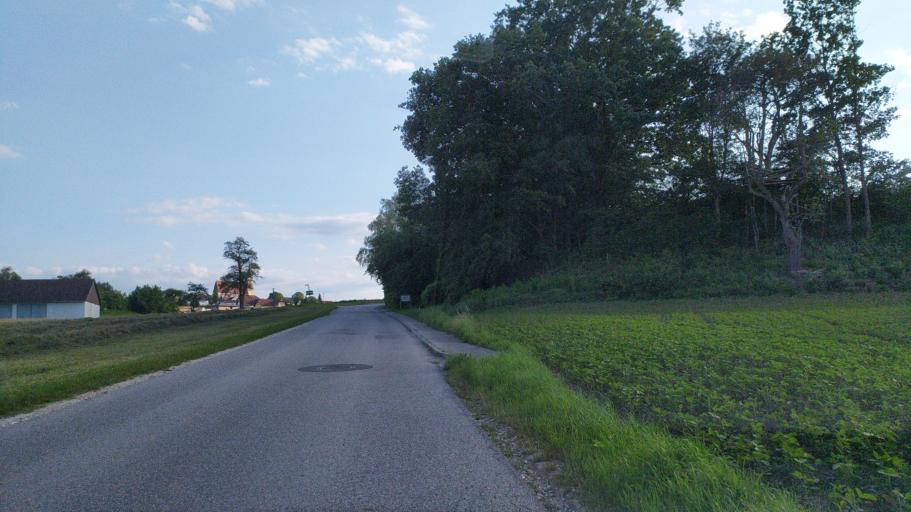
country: AT
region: Lower Austria
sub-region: Politischer Bezirk Amstetten
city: Zeillern
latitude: 48.1647
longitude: 14.7216
